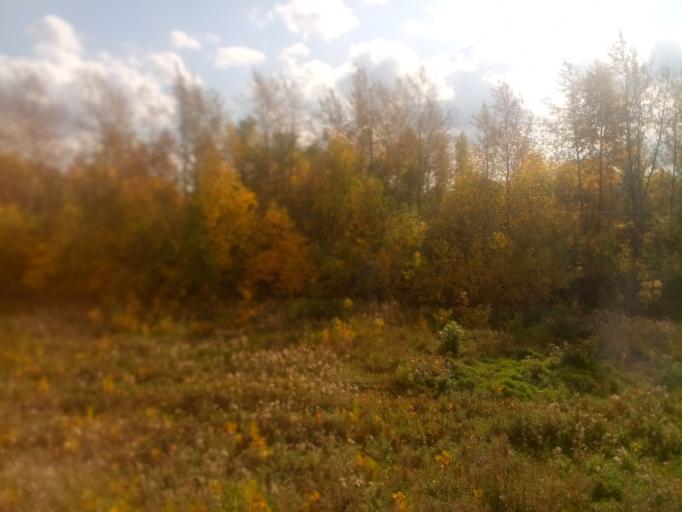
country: RU
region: Chuvashia
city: Urmary
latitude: 55.6923
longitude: 47.9589
